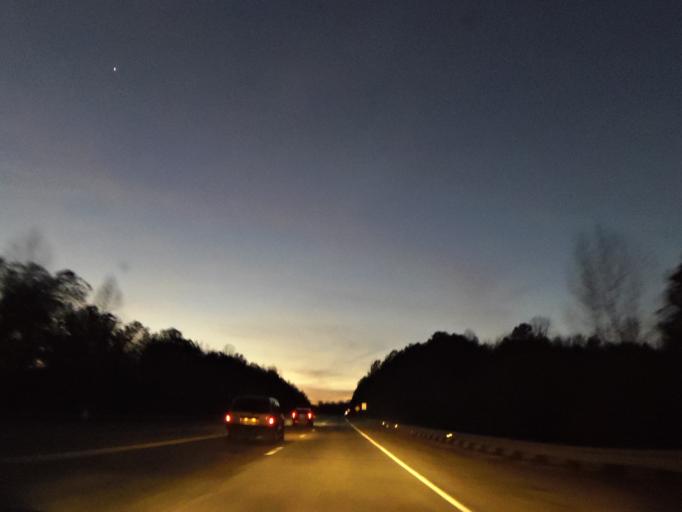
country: US
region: Georgia
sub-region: Whitfield County
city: Dalton
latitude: 34.8010
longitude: -84.9835
